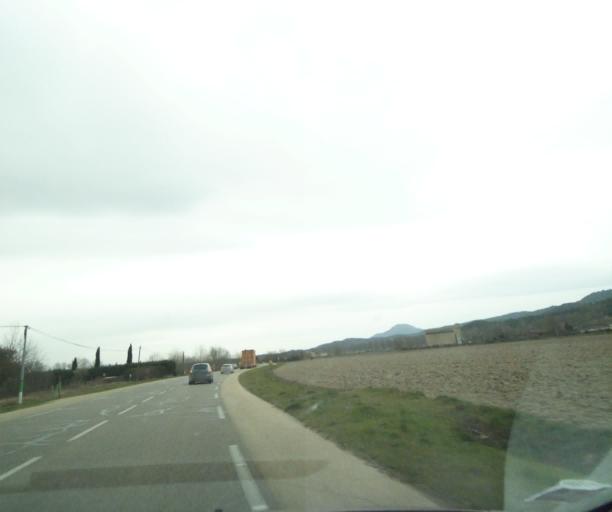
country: FR
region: Provence-Alpes-Cote d'Azur
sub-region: Departement des Bouches-du-Rhone
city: Meyrargues
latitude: 43.6495
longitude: 5.5408
